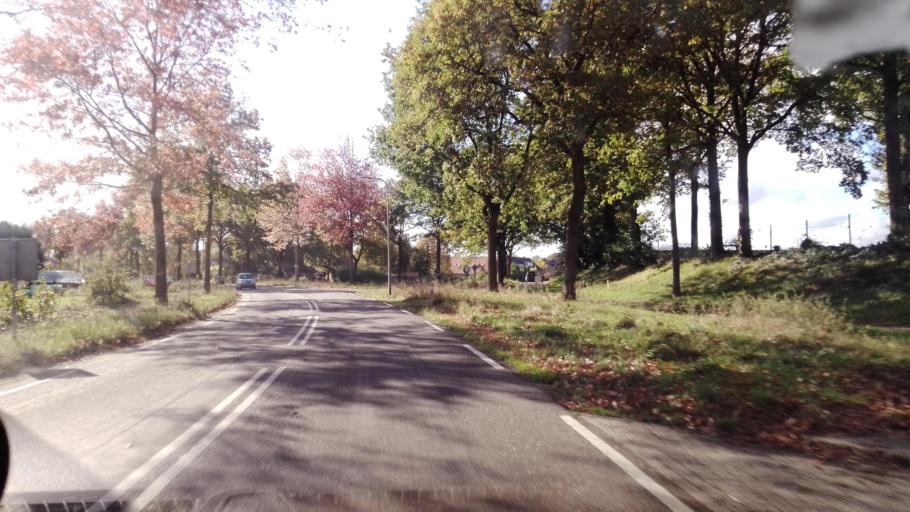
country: NL
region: Limburg
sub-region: Gemeente Venlo
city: Arcen
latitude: 51.4483
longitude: 6.1510
